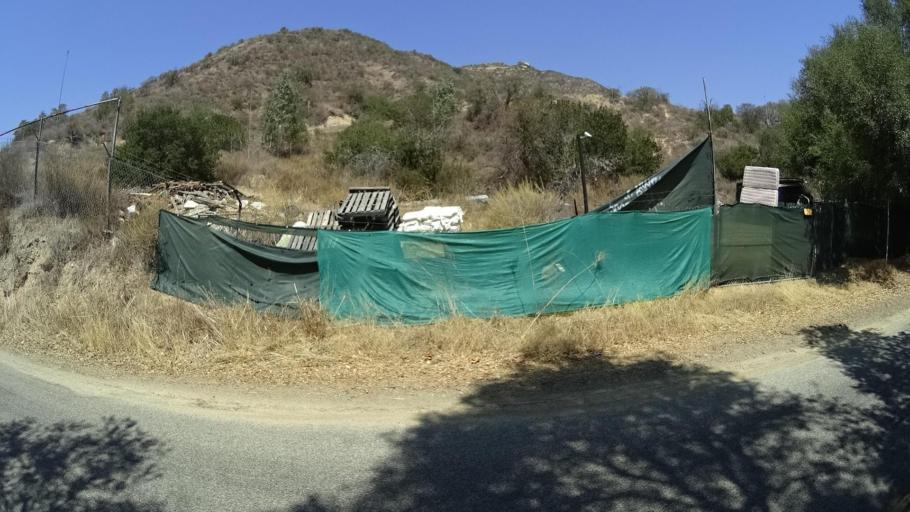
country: US
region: California
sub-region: San Diego County
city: Fallbrook
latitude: 33.4637
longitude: -117.2826
